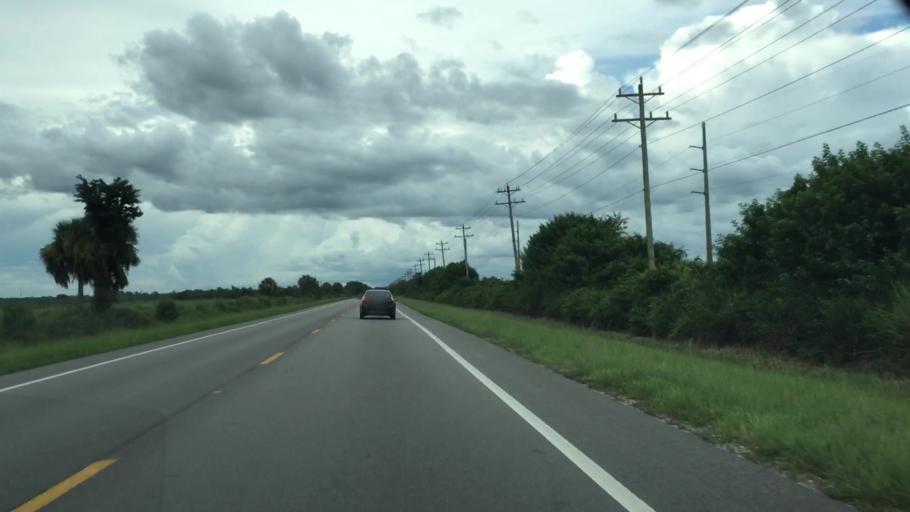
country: US
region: Florida
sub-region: Collier County
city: Immokalee
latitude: 26.3790
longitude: -81.4170
